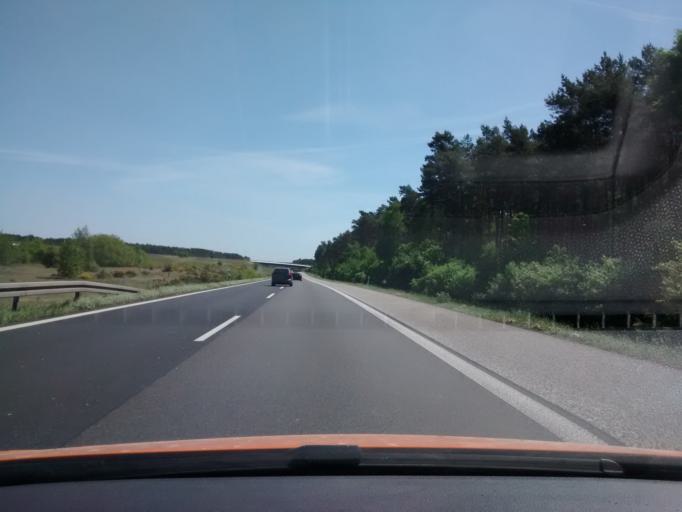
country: DE
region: Brandenburg
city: Erkner
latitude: 52.3236
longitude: 13.7410
